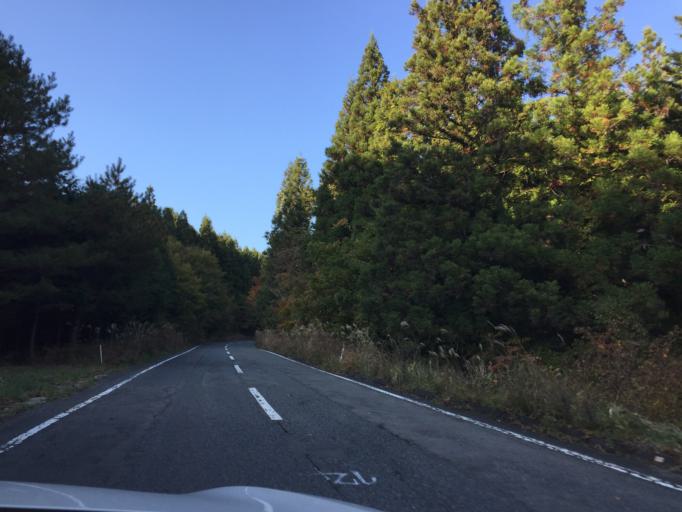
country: JP
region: Fukushima
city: Funehikimachi-funehiki
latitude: 37.2752
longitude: 140.7643
